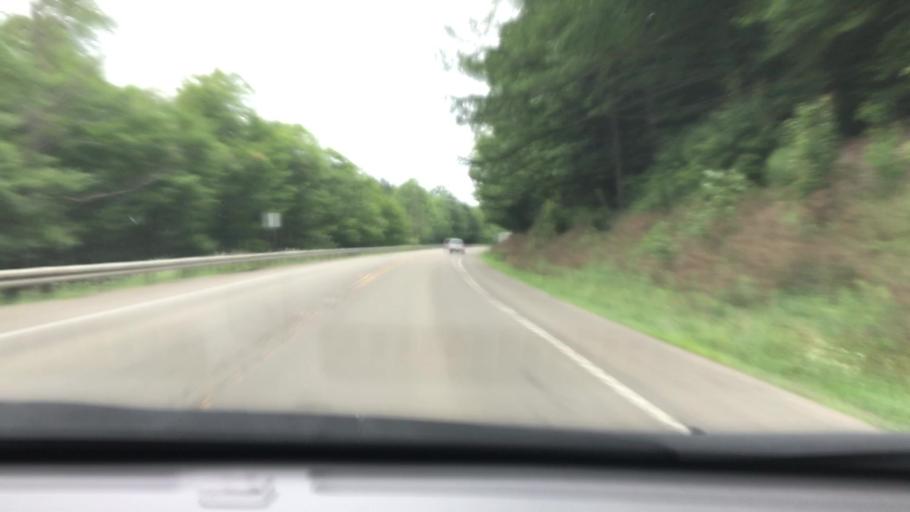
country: US
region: Pennsylvania
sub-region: McKean County
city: Kane
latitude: 41.6606
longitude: -78.6815
